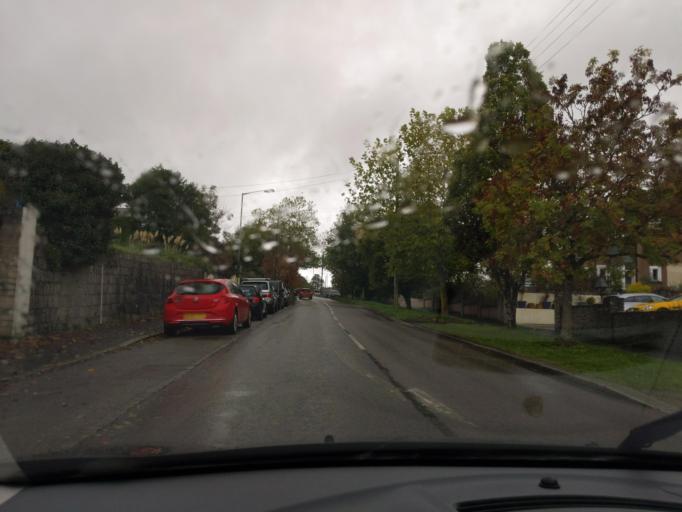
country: GB
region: England
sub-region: Cornwall
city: Wadebridge
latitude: 50.5172
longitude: -4.8429
